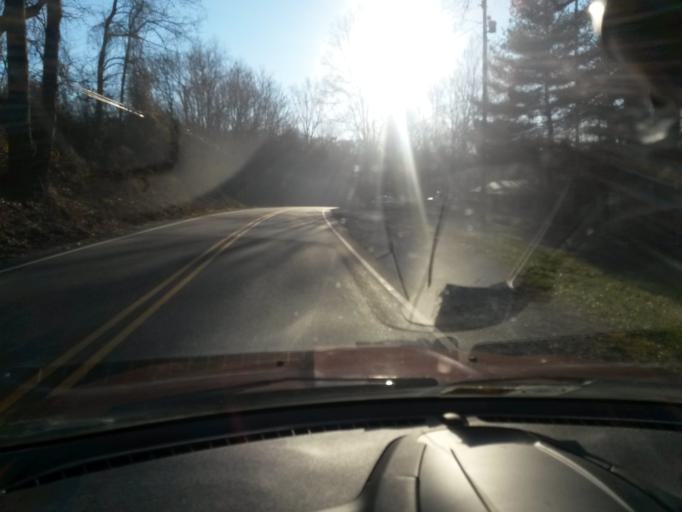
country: US
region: Virginia
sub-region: Amherst County
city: Amherst
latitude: 37.6189
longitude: -79.0944
